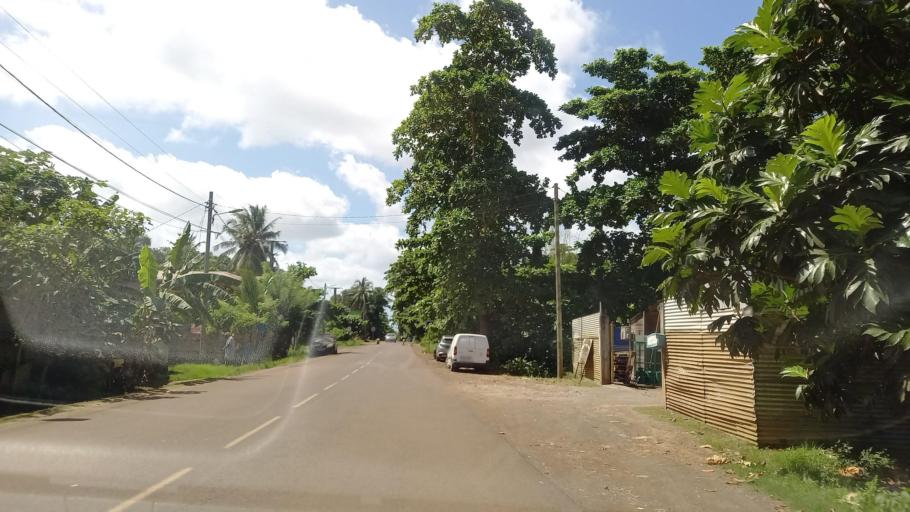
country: YT
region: Bandraboua
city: Bandraboua
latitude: -12.7224
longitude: 45.1230
